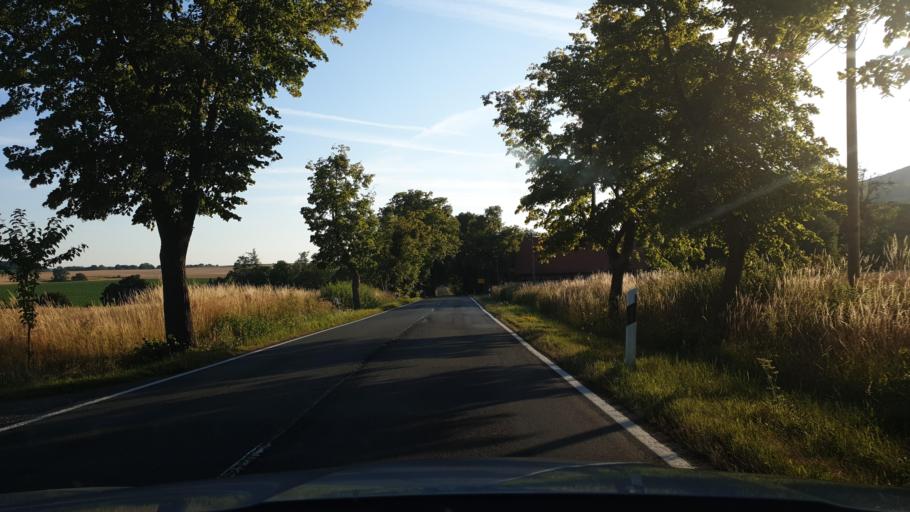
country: DE
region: Lower Saxony
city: Rehren
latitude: 52.2640
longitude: 9.2801
